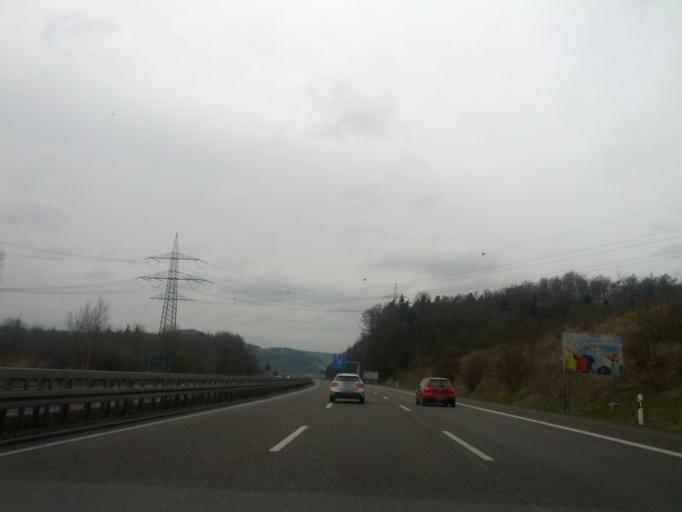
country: DE
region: Hesse
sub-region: Regierungsbezirk Kassel
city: Herleshausen
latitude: 51.0100
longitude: 10.2062
